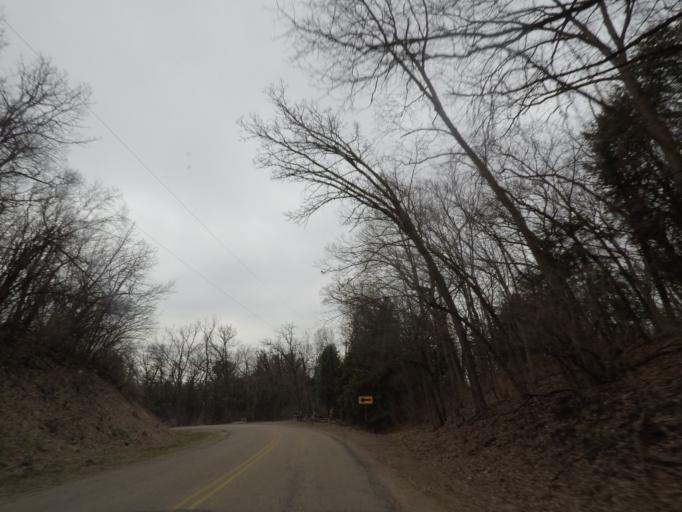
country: US
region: Wisconsin
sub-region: Dane County
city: Middleton
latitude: 43.1060
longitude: -89.5424
